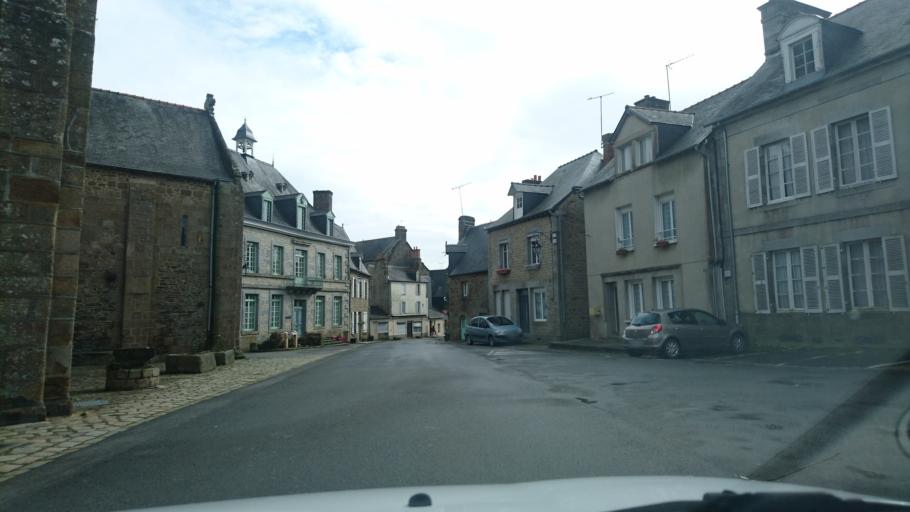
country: FR
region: Brittany
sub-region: Departement d'Ille-et-Vilaine
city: Antrain
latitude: 48.4614
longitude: -1.4860
